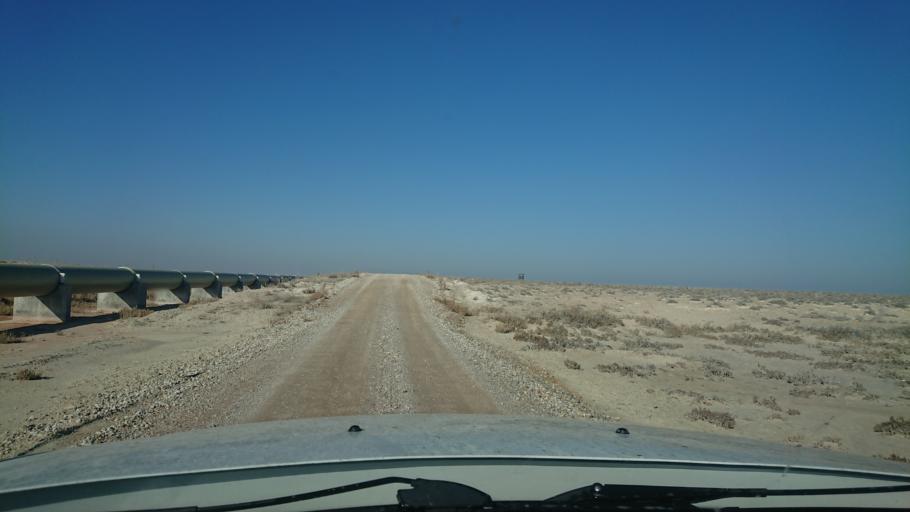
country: TR
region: Aksaray
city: Eskil
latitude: 38.4200
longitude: 33.5023
